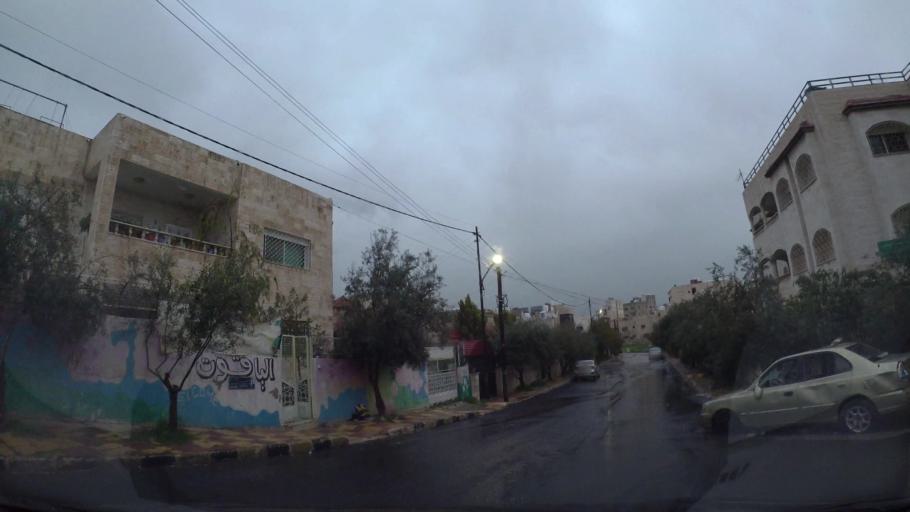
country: JO
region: Amman
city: Amman
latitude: 32.0013
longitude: 35.9645
